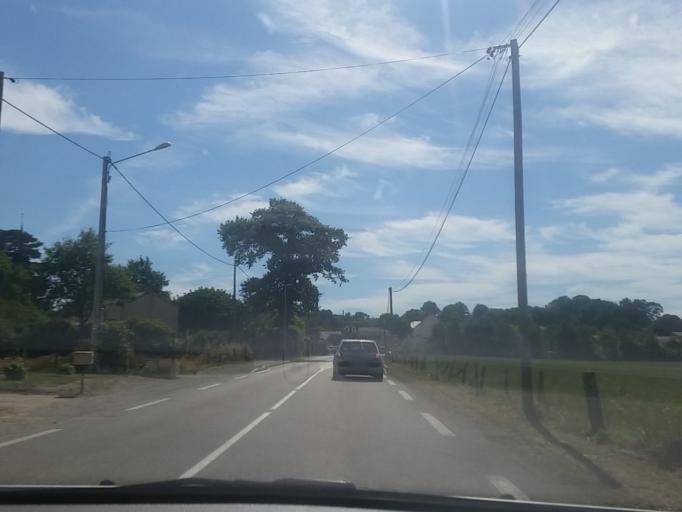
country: FR
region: Pays de la Loire
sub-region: Departement de la Loire-Atlantique
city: Chauve
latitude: 47.1891
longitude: -1.9451
